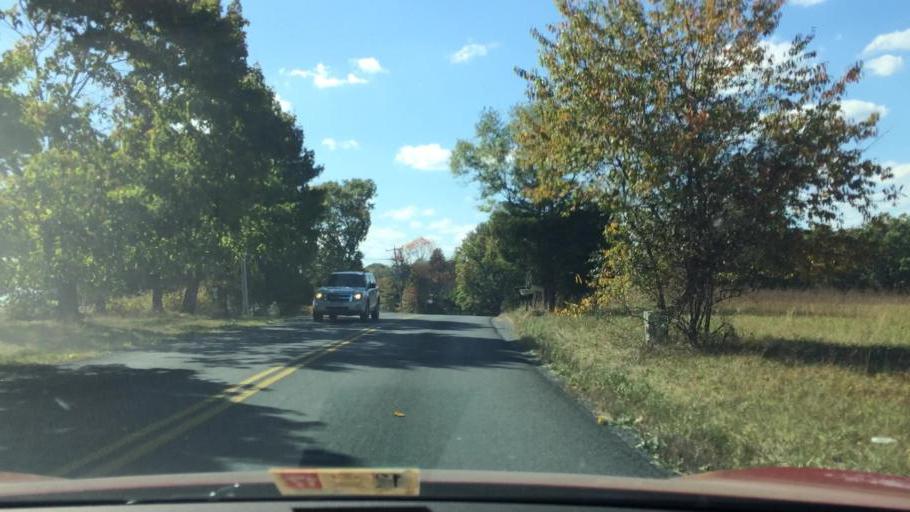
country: US
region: Virginia
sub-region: Frederick County
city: Shawnee Land
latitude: 39.3245
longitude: -78.3081
